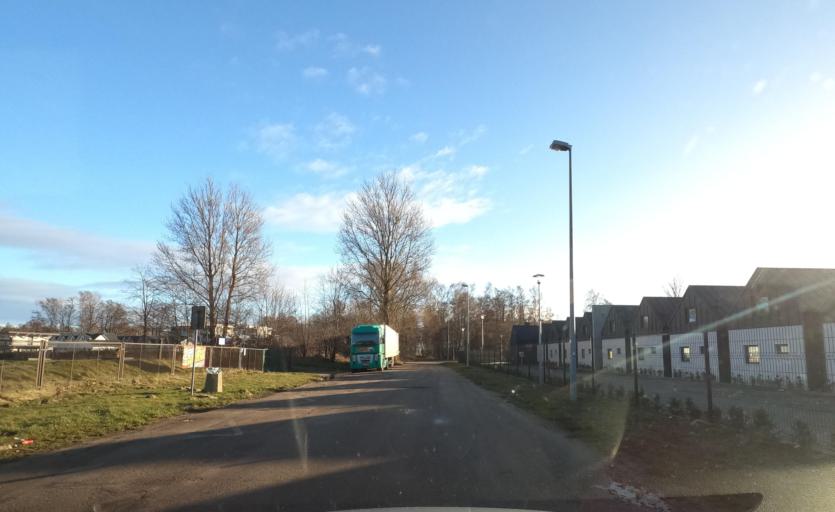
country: PL
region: West Pomeranian Voivodeship
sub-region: Powiat koszalinski
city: Mielno
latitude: 54.2708
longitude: 16.0968
